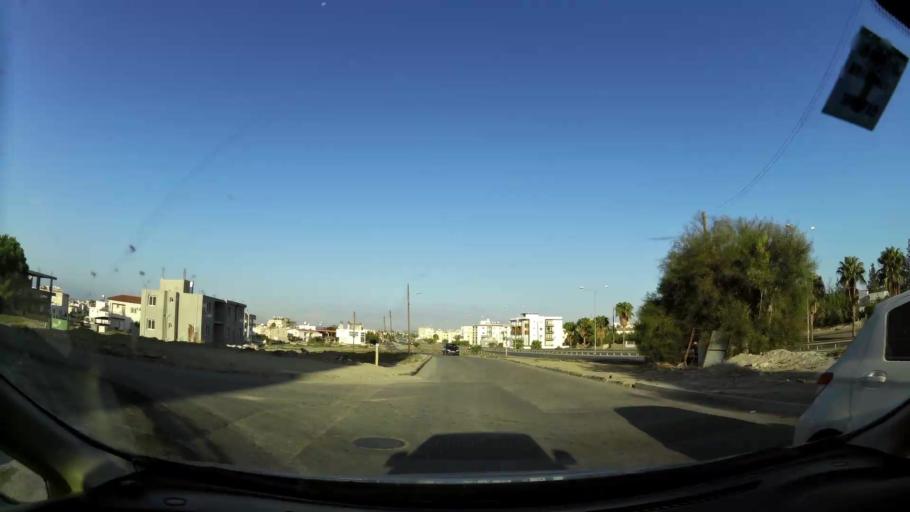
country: CY
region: Lefkosia
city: Nicosia
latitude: 35.2081
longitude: 33.3073
